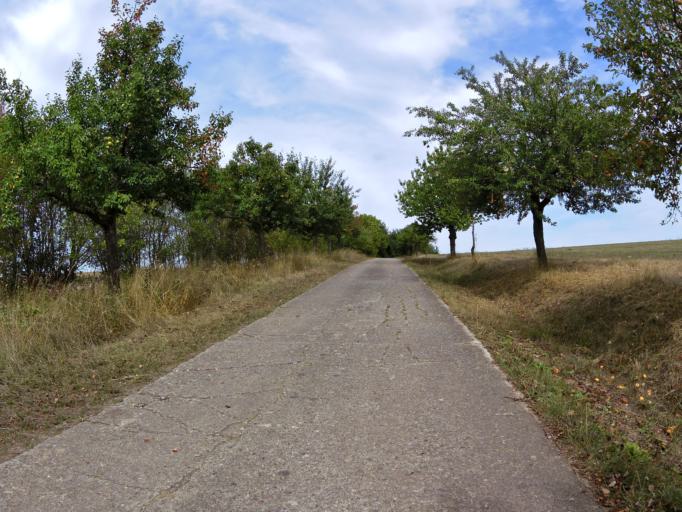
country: DE
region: Bavaria
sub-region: Regierungsbezirk Unterfranken
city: Waldbuttelbrunn
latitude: 49.7755
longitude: 9.8364
